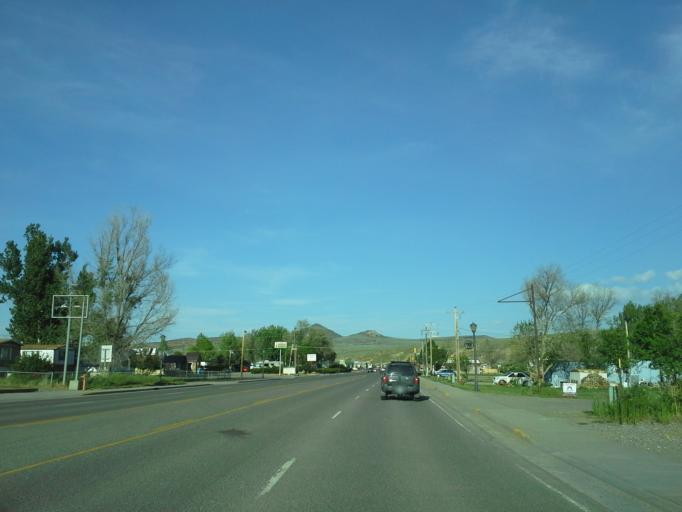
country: US
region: Wyoming
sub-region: Hot Springs County
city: Thermopolis
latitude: 43.6384
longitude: -108.2179
